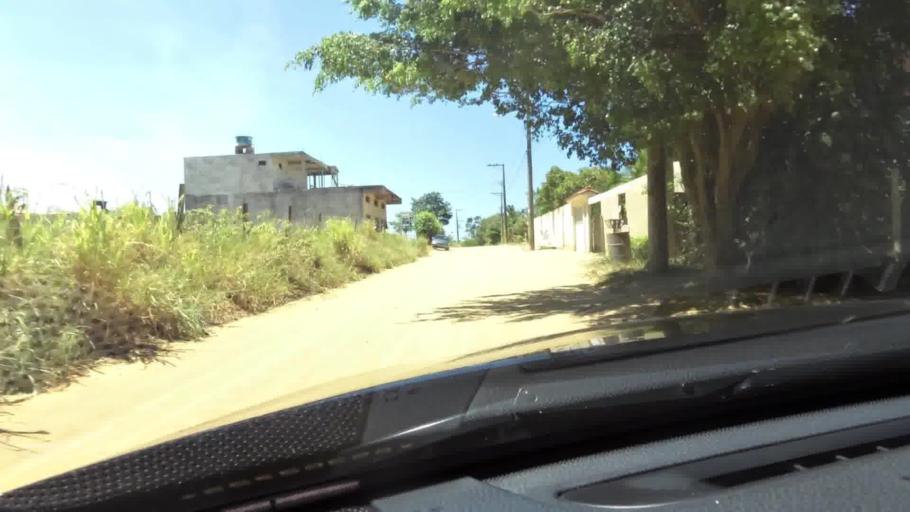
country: BR
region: Espirito Santo
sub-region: Guarapari
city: Guarapari
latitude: -20.6152
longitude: -40.4631
